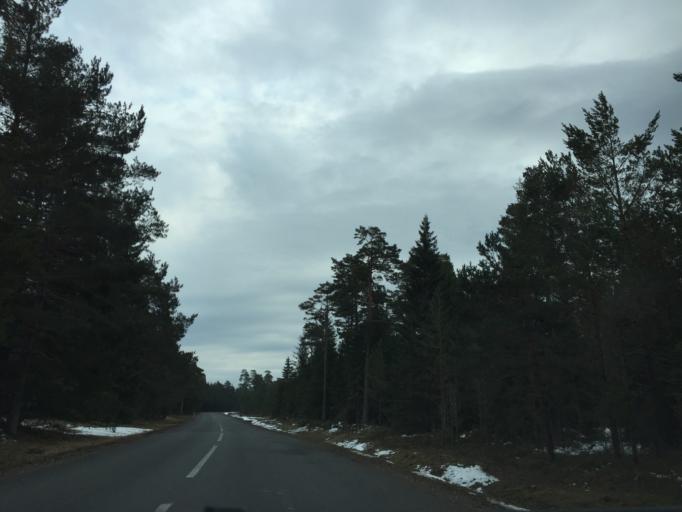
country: EE
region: Saare
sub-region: Kuressaare linn
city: Kuressaare
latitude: 58.4322
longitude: 22.0686
